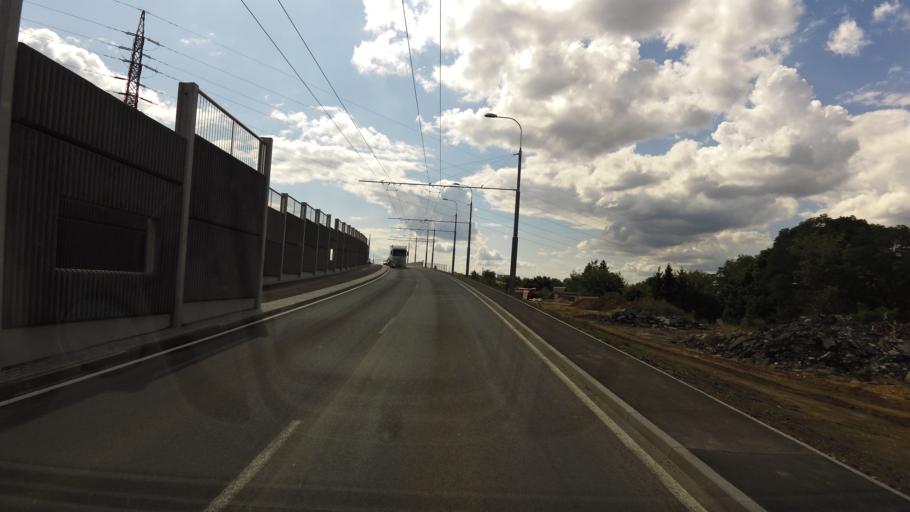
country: CZ
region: Plzensky
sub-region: Okres Plzen-Mesto
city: Pilsen
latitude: 49.7416
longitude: 13.3427
